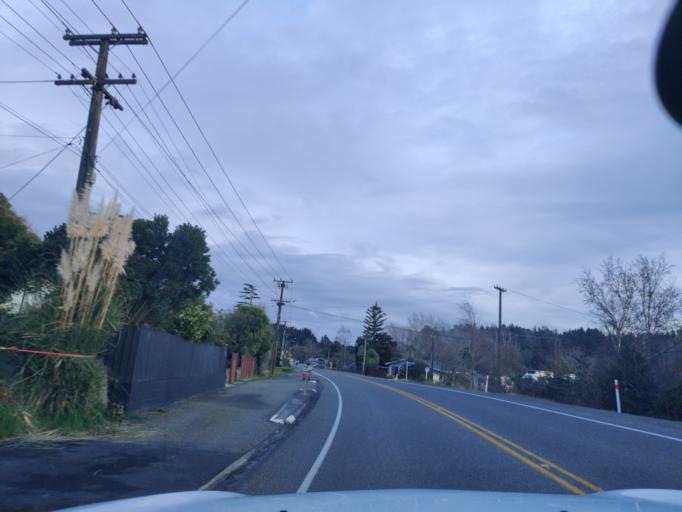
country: NZ
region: Manawatu-Wanganui
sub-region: Palmerston North City
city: Palmerston North
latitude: -40.3738
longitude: 175.6512
